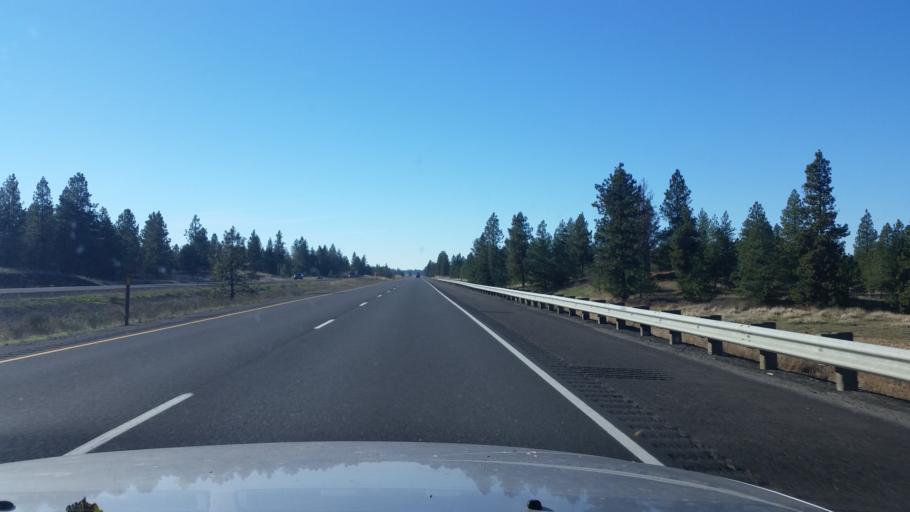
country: US
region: Washington
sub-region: Spokane County
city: Medical Lake
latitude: 47.4579
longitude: -117.7595
